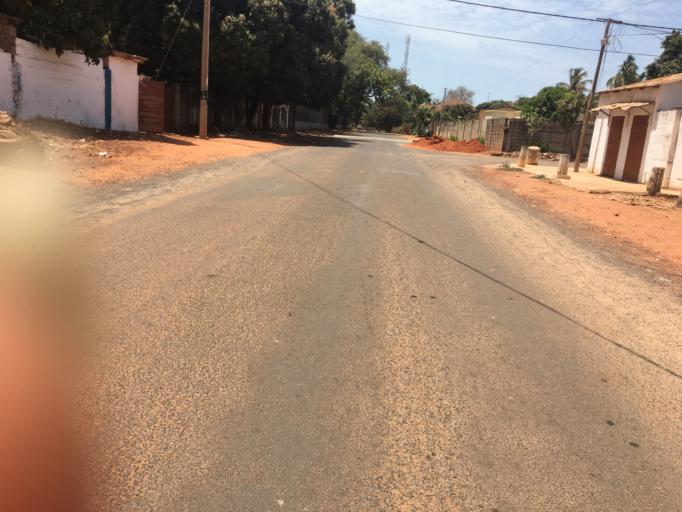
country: GM
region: Banjul
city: Bakau
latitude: 13.4731
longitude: -16.6848
